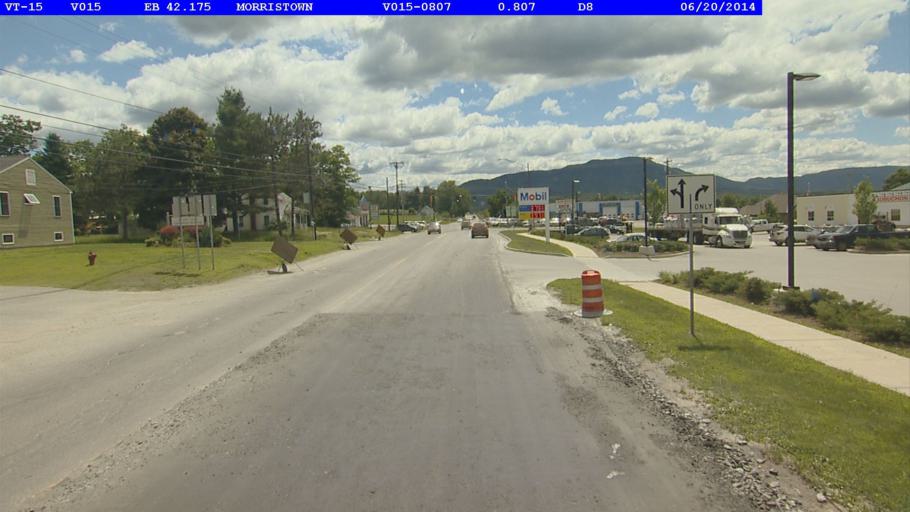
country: US
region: Vermont
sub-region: Lamoille County
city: Morrisville
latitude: 44.5762
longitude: -72.5935
